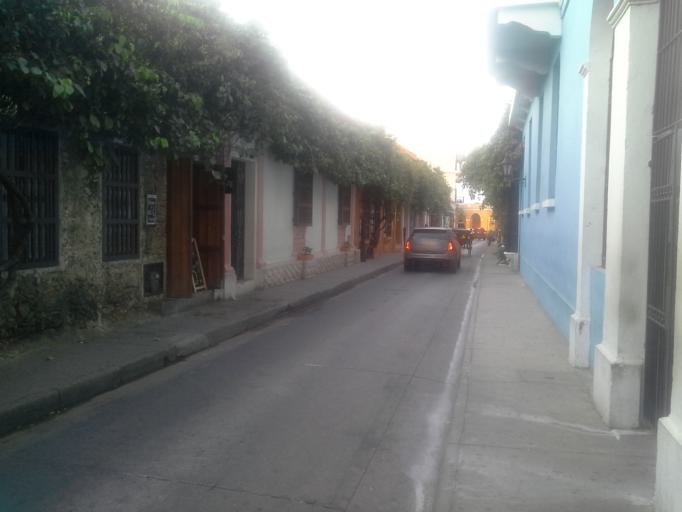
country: CO
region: Bolivar
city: Cartagena
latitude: 10.4285
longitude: -75.5472
